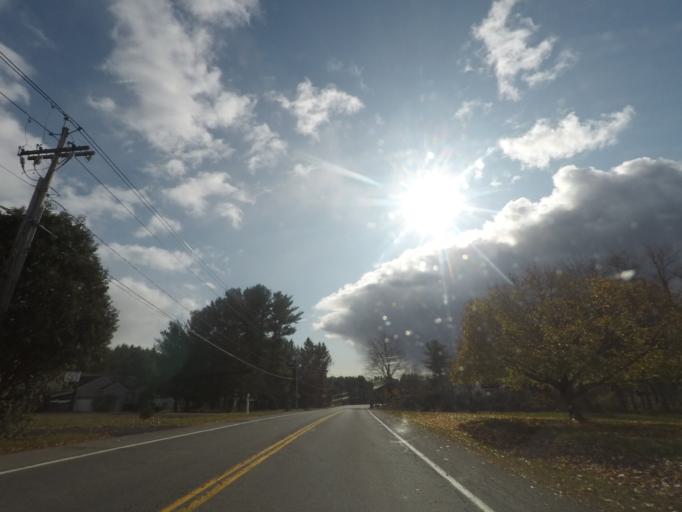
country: US
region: New York
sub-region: Saratoga County
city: Country Knolls
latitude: 42.9005
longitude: -73.8189
